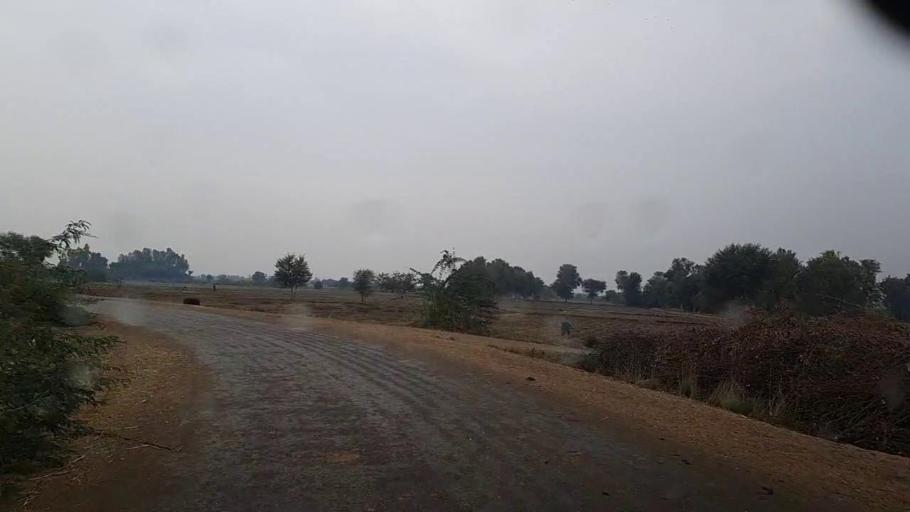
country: PK
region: Sindh
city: Ranipur
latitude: 27.2590
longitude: 68.5752
